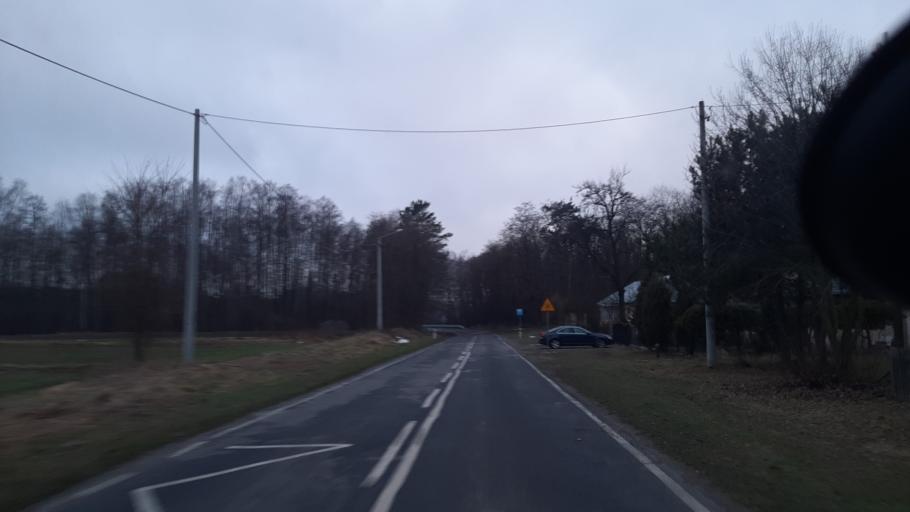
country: PL
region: Lublin Voivodeship
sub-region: Powiat parczewski
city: Debowa Kloda
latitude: 51.6394
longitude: 23.0265
